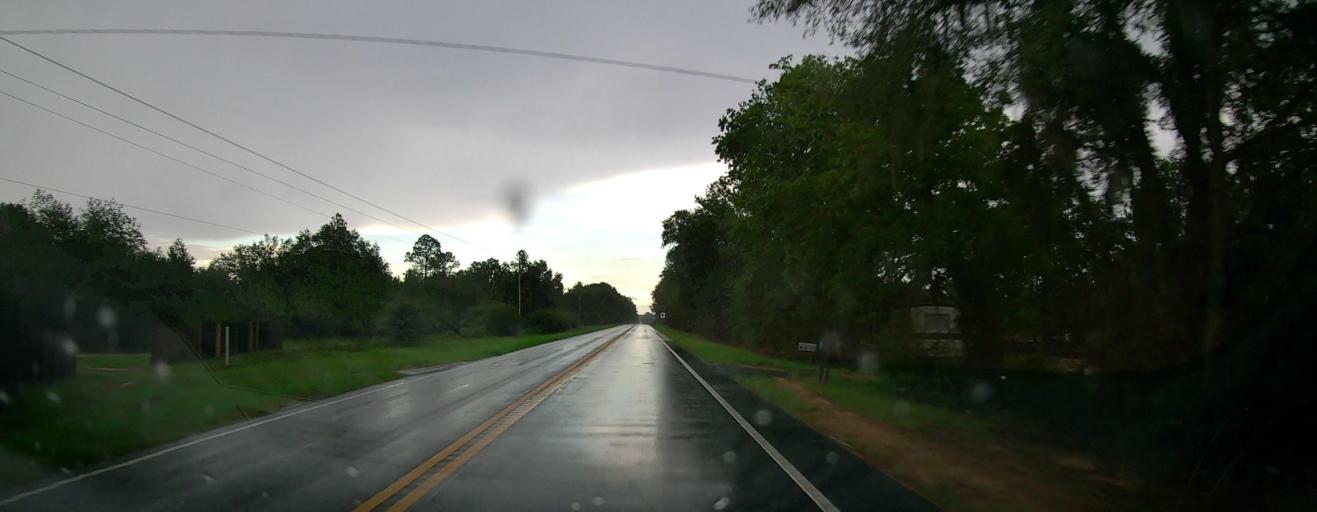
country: US
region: Georgia
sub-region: Glynn County
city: Dock Junction
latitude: 31.3102
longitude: -81.7306
